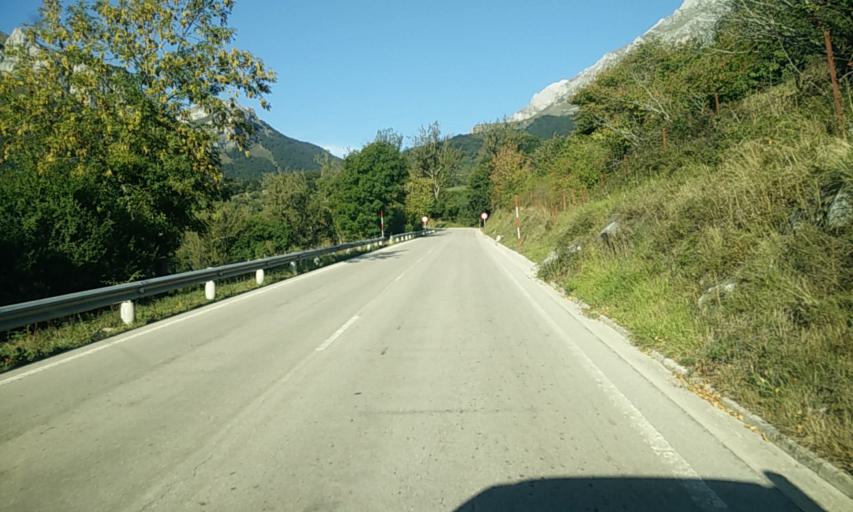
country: ES
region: Cantabria
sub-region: Provincia de Cantabria
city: Camaleno
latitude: 43.1306
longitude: -4.7989
